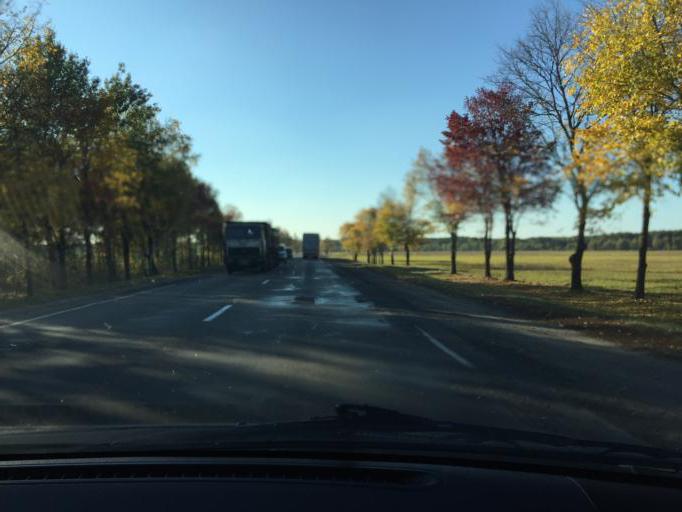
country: BY
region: Brest
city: Luninyets
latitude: 52.2753
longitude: 26.8821
